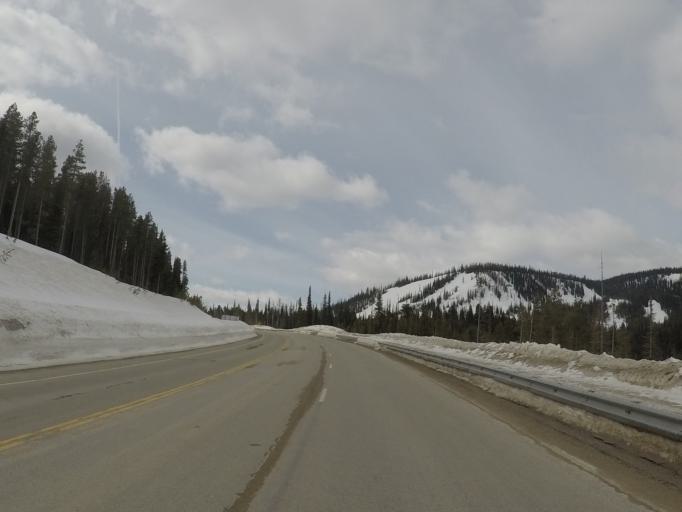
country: US
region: Idaho
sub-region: Lemhi County
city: Salmon
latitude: 45.6984
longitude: -113.9472
